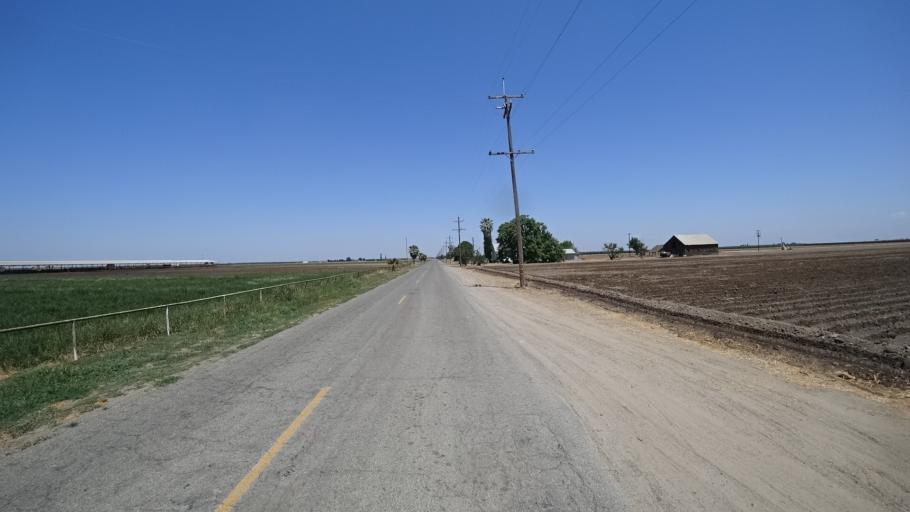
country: US
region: California
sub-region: Kings County
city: Armona
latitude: 36.3592
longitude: -119.7269
